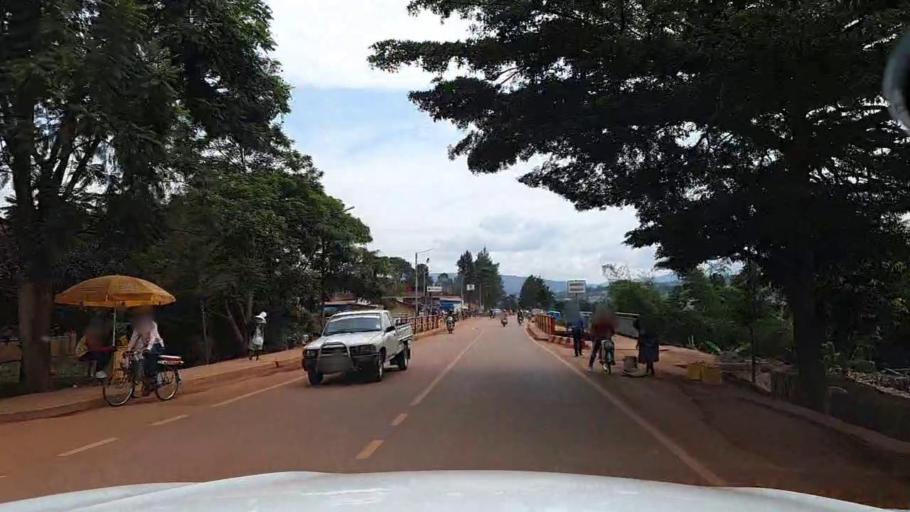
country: RW
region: Kigali
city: Kigali
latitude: -1.9037
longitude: 30.0512
